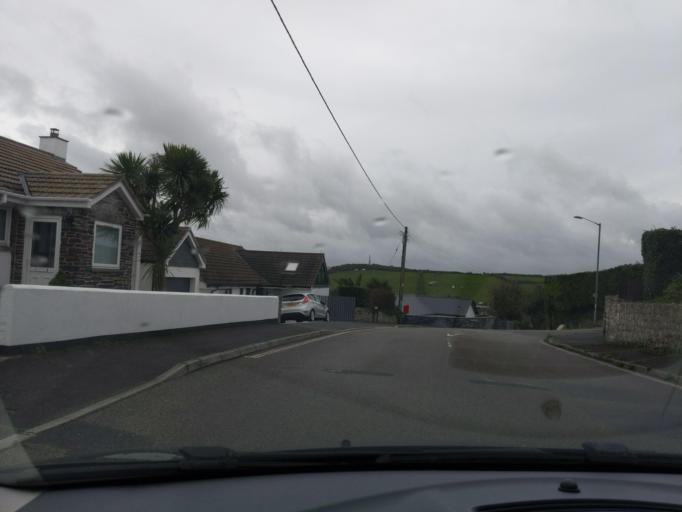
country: GB
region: England
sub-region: Cornwall
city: Padstow
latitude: 50.5364
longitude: -4.9367
